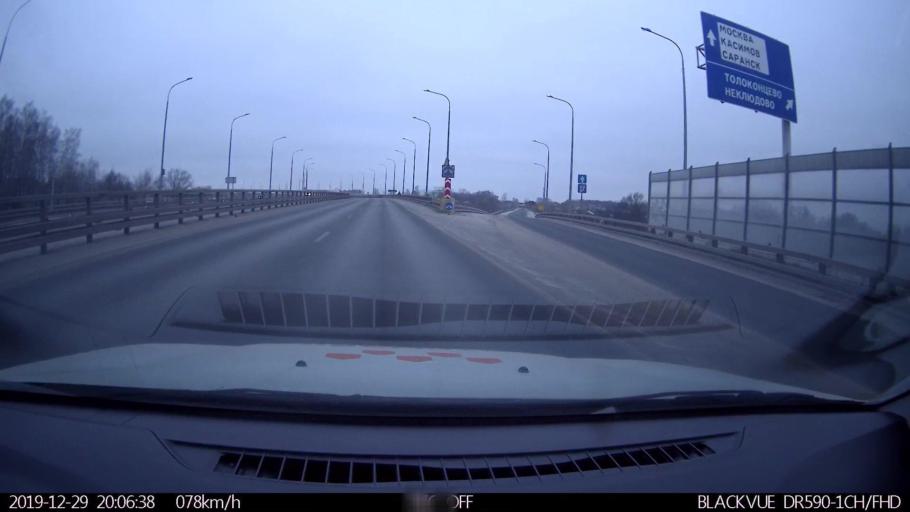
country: RU
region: Nizjnij Novgorod
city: Neklyudovo
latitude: 56.3967
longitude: 43.9980
